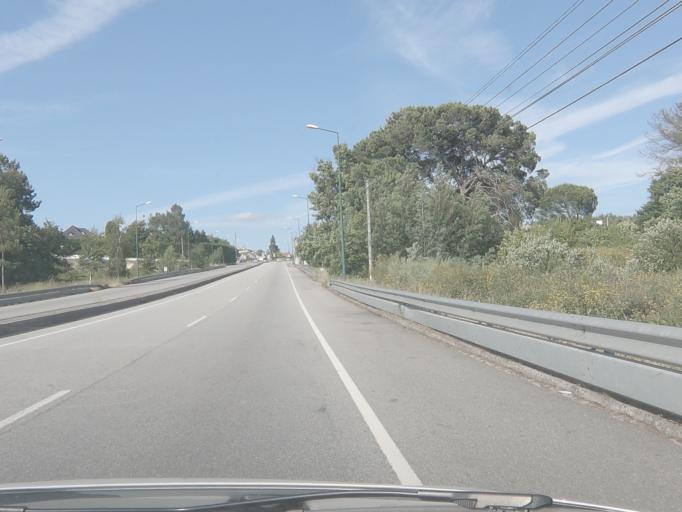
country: PT
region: Viseu
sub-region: Viseu
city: Viseu
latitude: 40.6316
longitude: -7.9335
